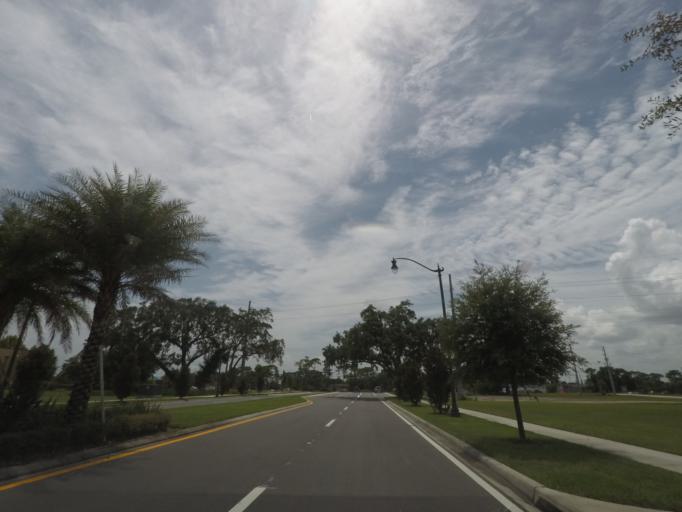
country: US
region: Florida
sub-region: Osceola County
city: Celebration
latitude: 28.3336
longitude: -81.4750
